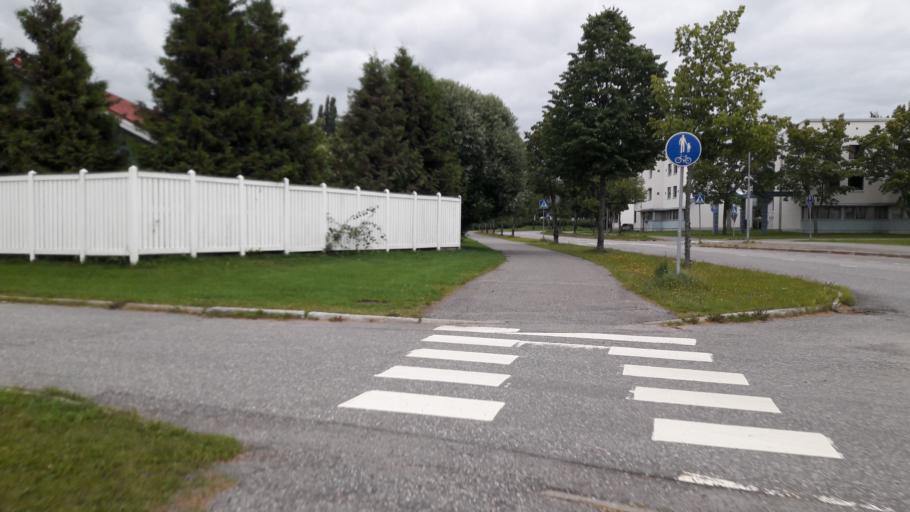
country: FI
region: North Karelia
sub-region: Joensuu
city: Joensuu
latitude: 62.6198
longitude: 29.6936
